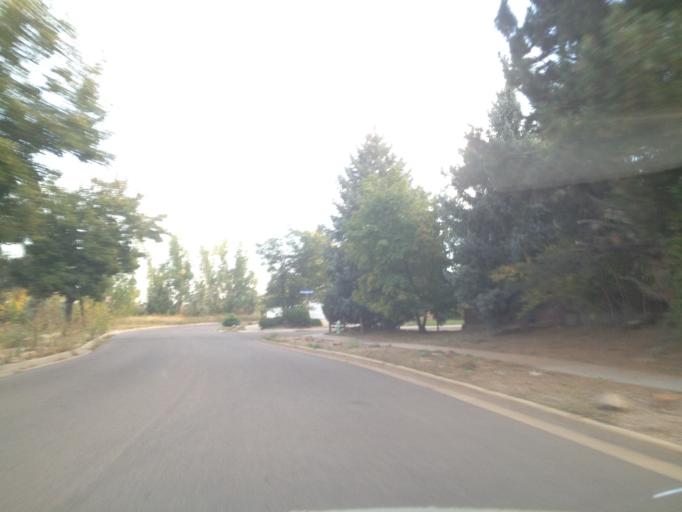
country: US
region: Colorado
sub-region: Boulder County
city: Boulder
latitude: 39.9985
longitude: -105.2252
